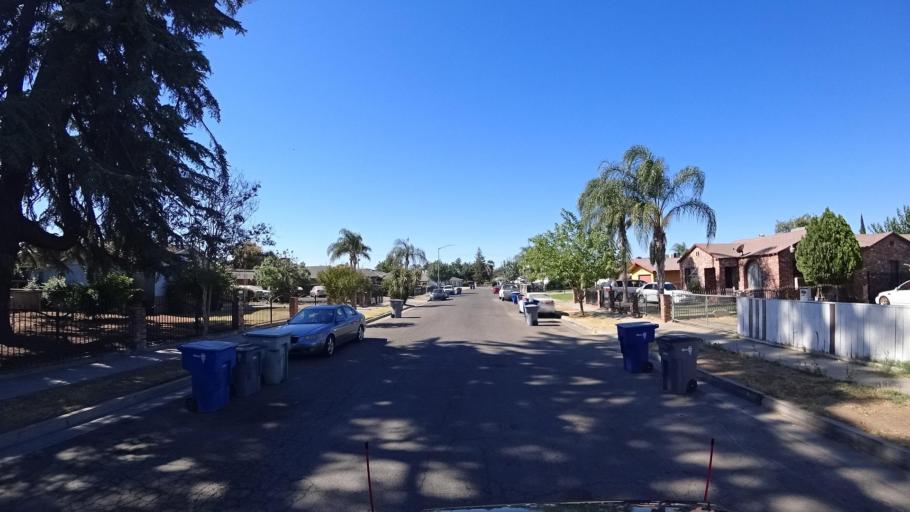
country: US
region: California
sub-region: Fresno County
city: Fresno
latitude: 36.7155
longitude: -119.7897
